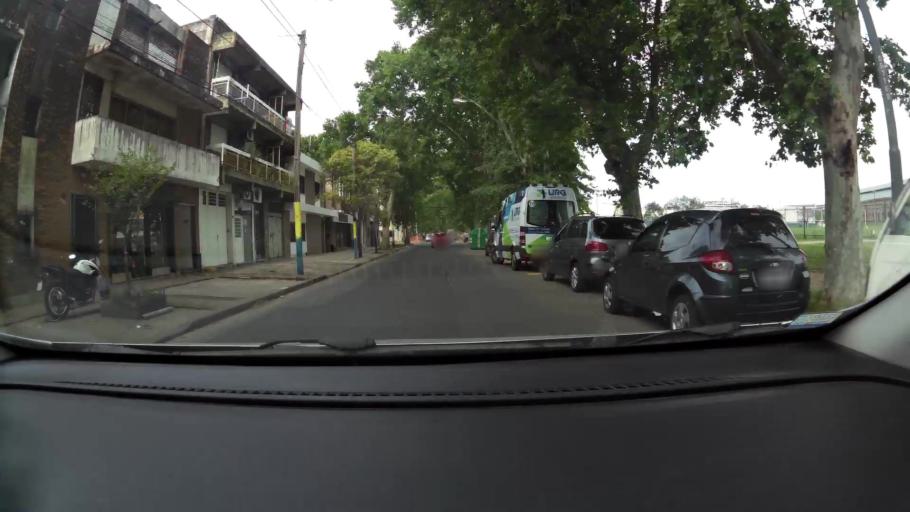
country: AR
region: Santa Fe
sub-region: Departamento de Rosario
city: Rosario
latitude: -32.9265
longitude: -60.6729
